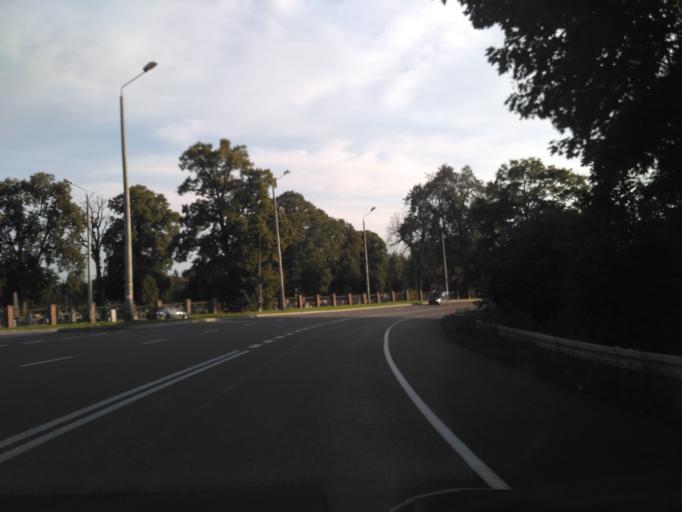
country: PL
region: Lublin Voivodeship
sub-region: Powiat lubelski
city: Bychawa
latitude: 51.0218
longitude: 22.5367
